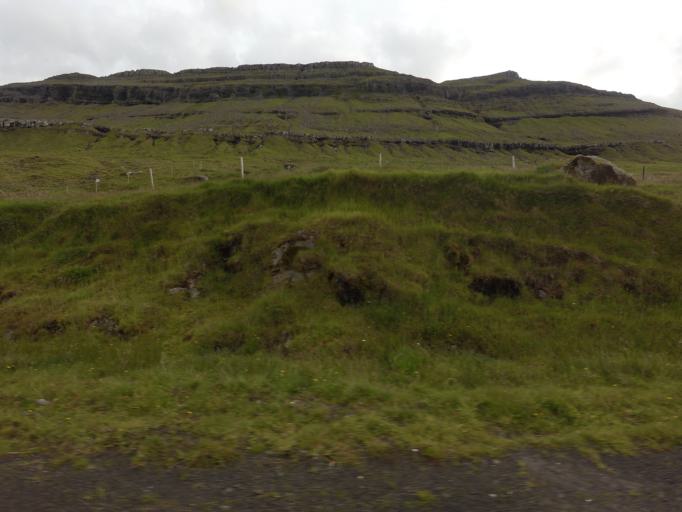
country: FO
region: Streymoy
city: Kollafjordhur
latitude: 62.1430
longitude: -6.9024
